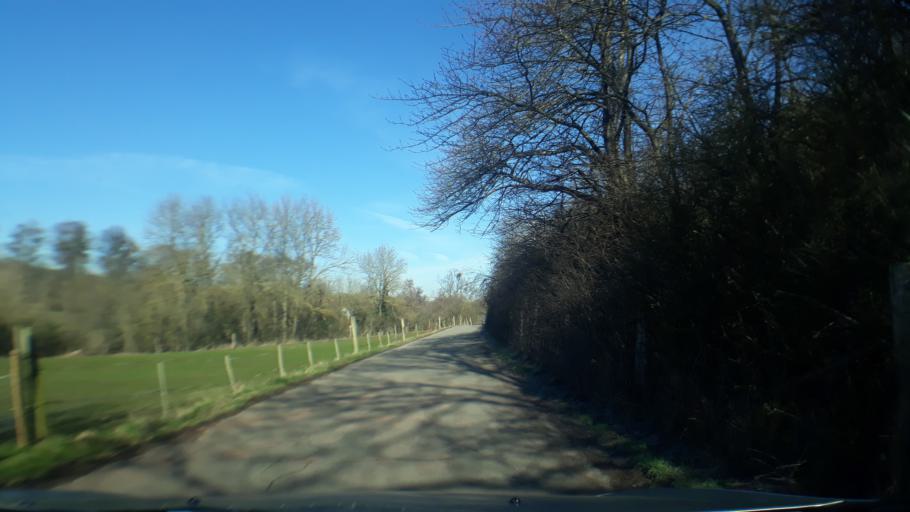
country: DE
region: North Rhine-Westphalia
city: Heimbach
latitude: 50.6423
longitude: 6.5464
